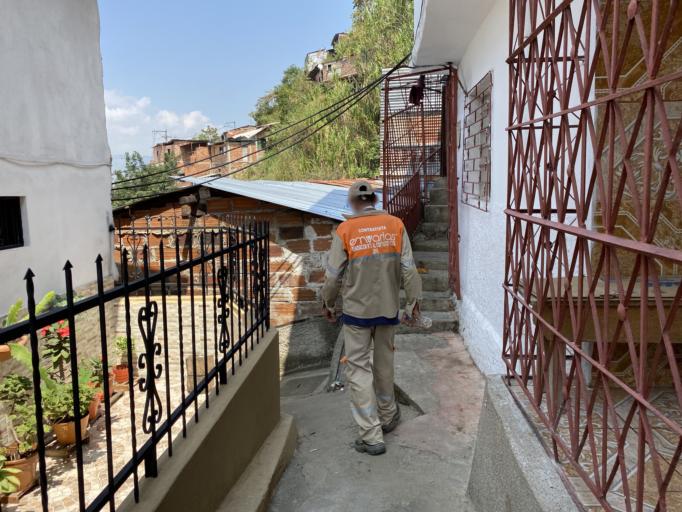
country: CO
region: Antioquia
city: Medellin
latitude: 6.2677
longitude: -75.5420
